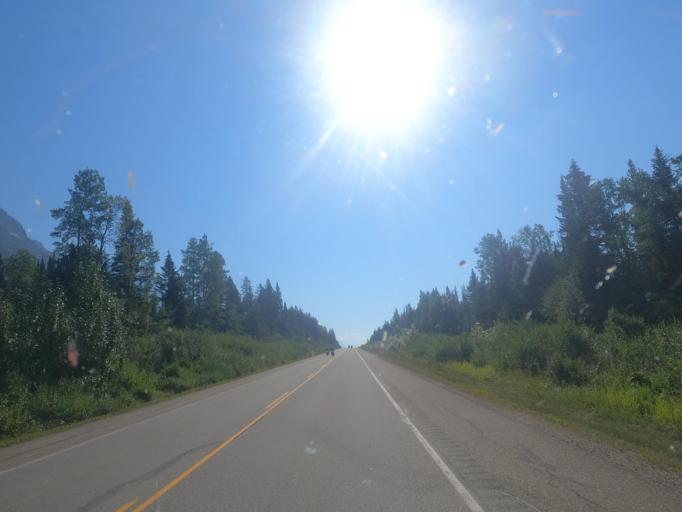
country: CA
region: Alberta
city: Jasper Park Lodge
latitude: 52.9783
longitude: -118.9707
